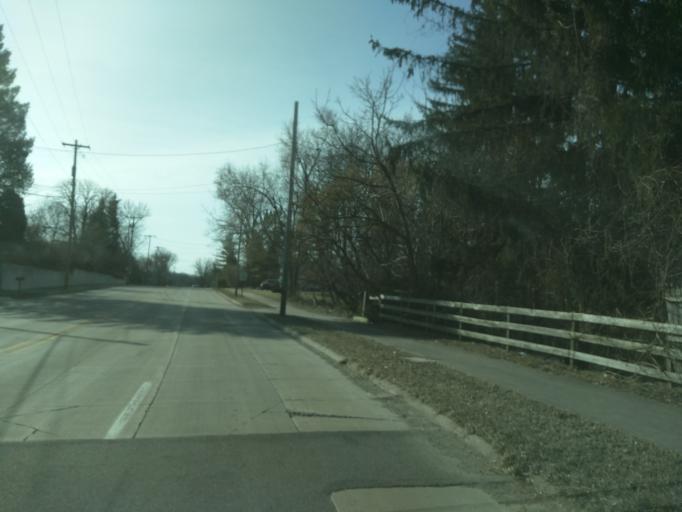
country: US
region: Michigan
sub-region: Ingham County
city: Haslett
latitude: 42.7614
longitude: -84.4125
